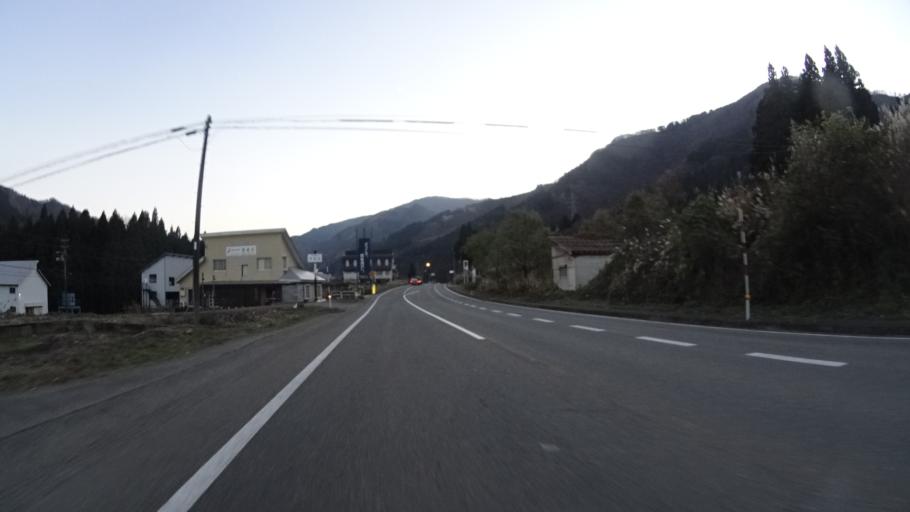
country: JP
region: Niigata
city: Shiozawa
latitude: 36.9639
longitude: 138.8012
